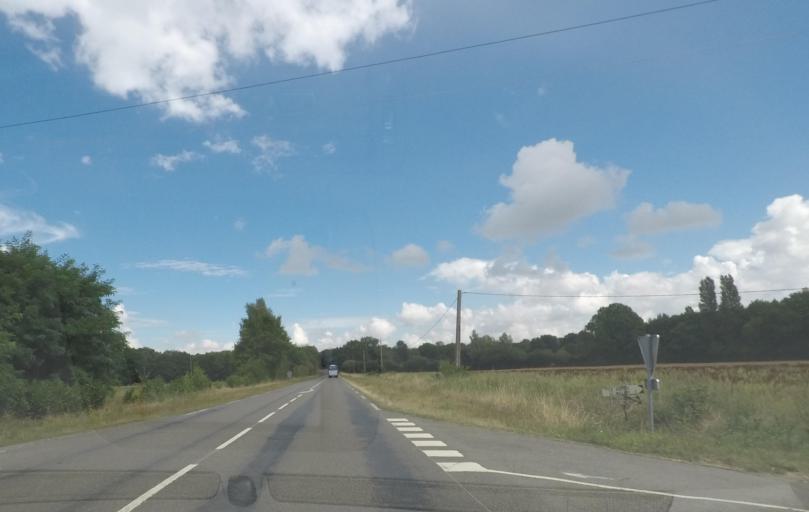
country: FR
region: Pays de la Loire
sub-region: Departement de la Sarthe
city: Beaufay
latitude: 48.1420
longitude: 0.3810
